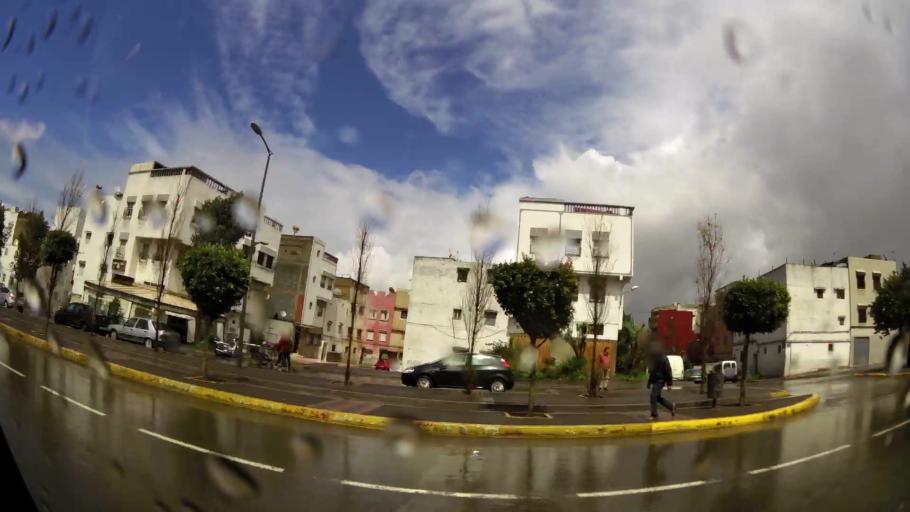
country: MA
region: Grand Casablanca
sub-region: Mediouna
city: Tit Mellil
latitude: 33.5525
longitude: -7.5531
